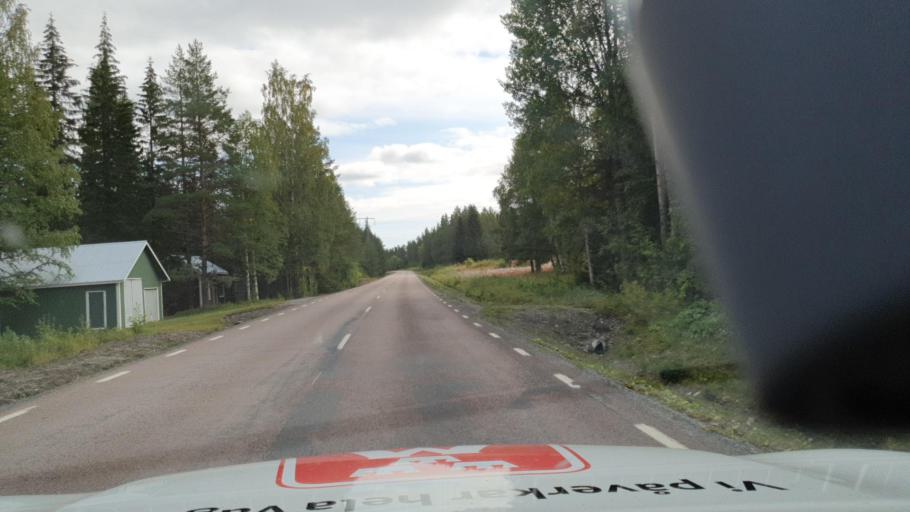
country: SE
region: Jaemtland
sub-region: Stroemsunds Kommun
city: Stroemsund
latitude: 63.7327
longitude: 15.7693
